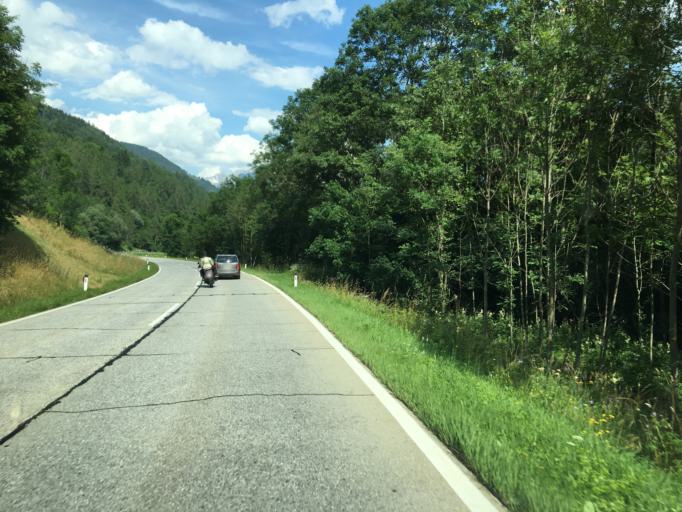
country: AT
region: Carinthia
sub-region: Politischer Bezirk Spittal an der Drau
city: Flattach
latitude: 46.9345
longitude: 13.0946
